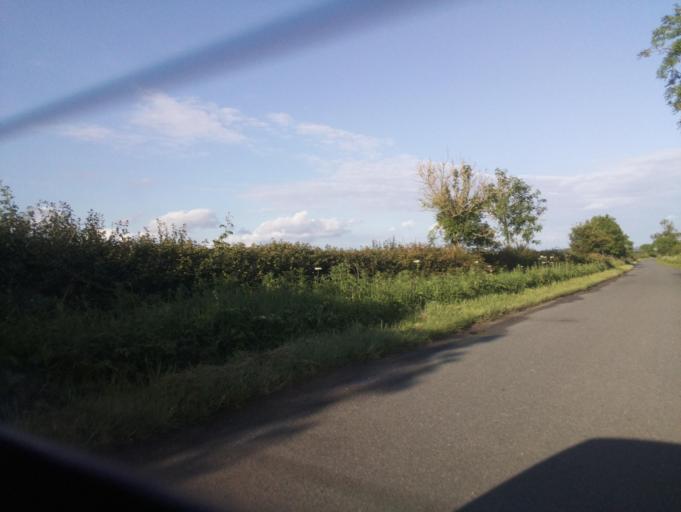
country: GB
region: England
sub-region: Lincolnshire
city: Navenby
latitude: 53.1152
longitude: -0.6169
